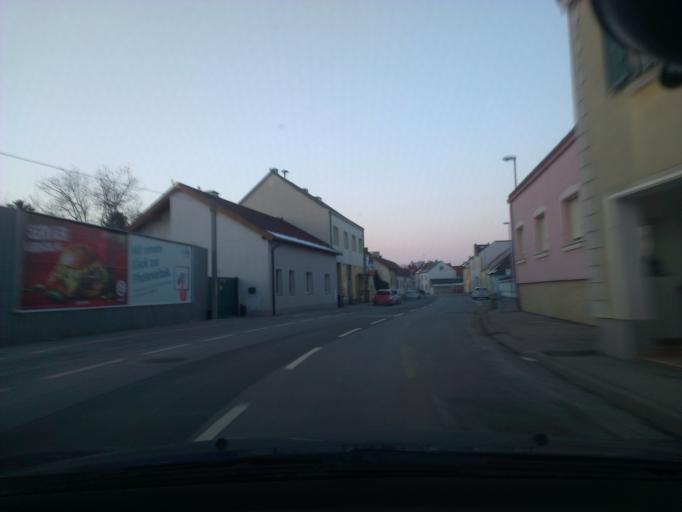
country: AT
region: Lower Austria
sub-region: Politischer Bezirk Bruck an der Leitha
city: Enzersdorf an der Fischa
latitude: 48.0865
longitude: 16.6087
